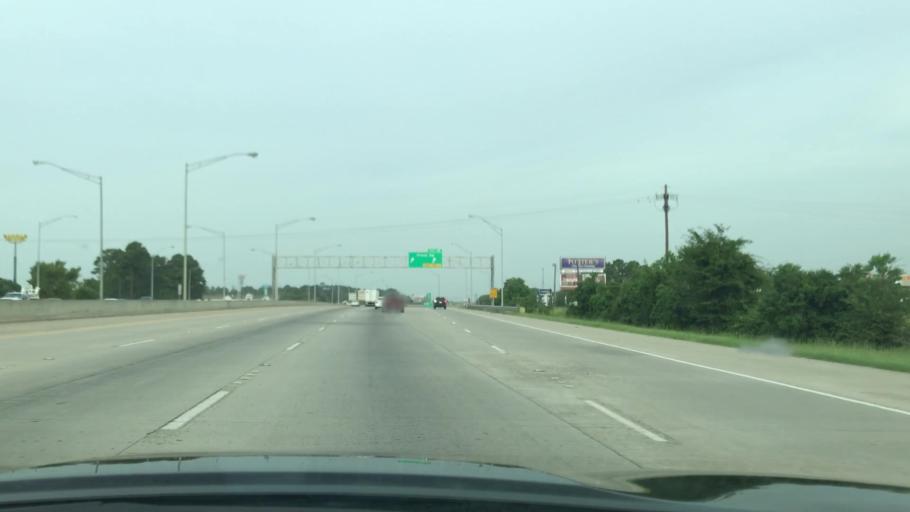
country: US
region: Louisiana
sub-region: Caddo Parish
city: Greenwood
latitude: 32.4516
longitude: -93.8598
